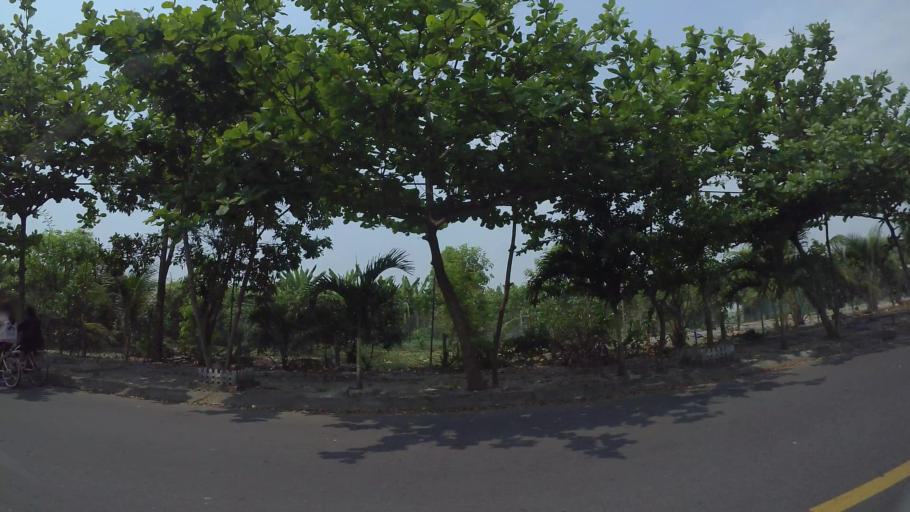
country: VN
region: Da Nang
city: Cam Le
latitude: 15.9911
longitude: 108.2136
